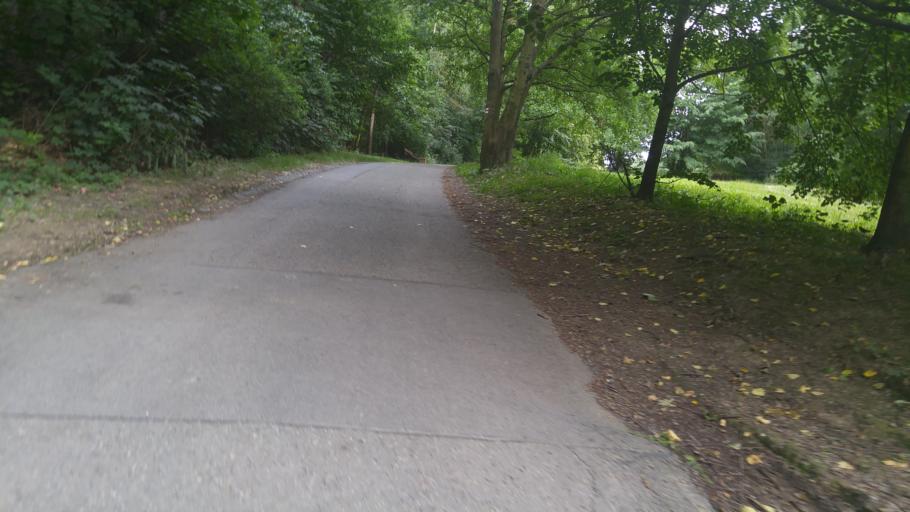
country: CZ
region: Central Bohemia
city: Horomerice
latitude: 50.1008
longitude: 14.3369
